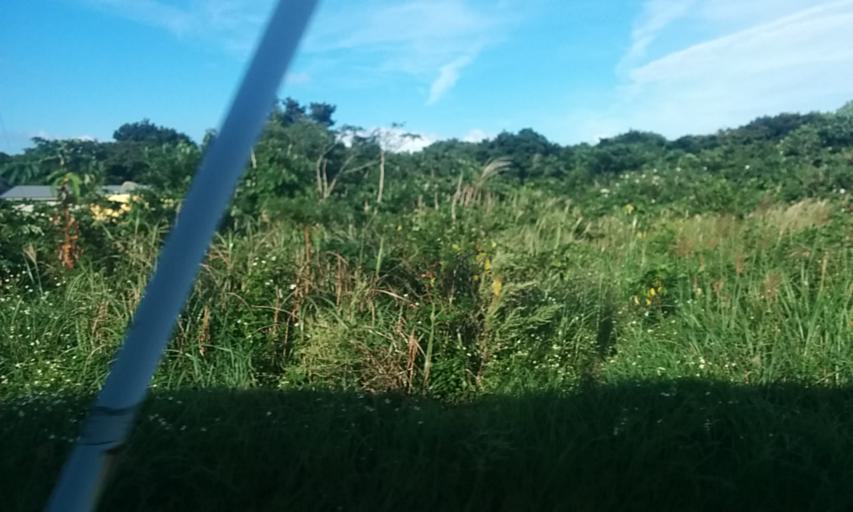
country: JP
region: Kagoshima
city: Nishinoomote
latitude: 30.3809
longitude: 130.6608
